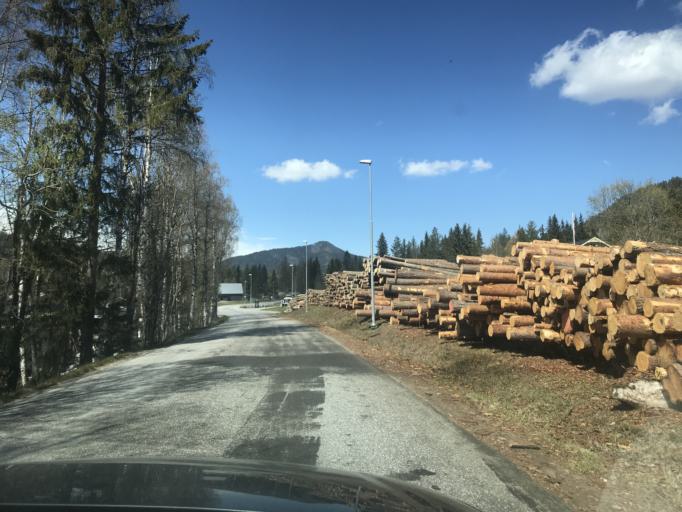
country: NO
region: Telemark
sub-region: Hjartdal
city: Sauland
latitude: 59.7151
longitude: 8.8530
